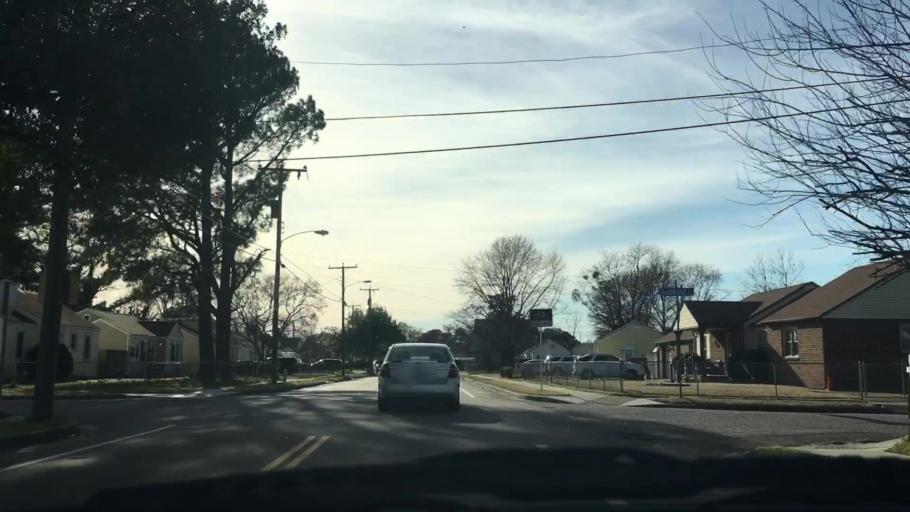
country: US
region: Virginia
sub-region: City of Norfolk
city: Norfolk
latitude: 36.8777
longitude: -76.2352
